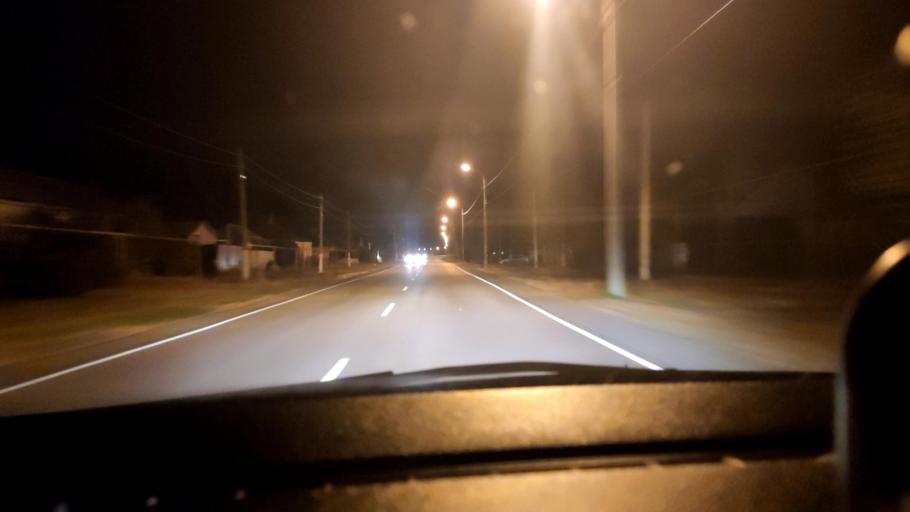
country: RU
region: Voronezj
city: Shilovo
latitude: 51.5758
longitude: 39.0391
